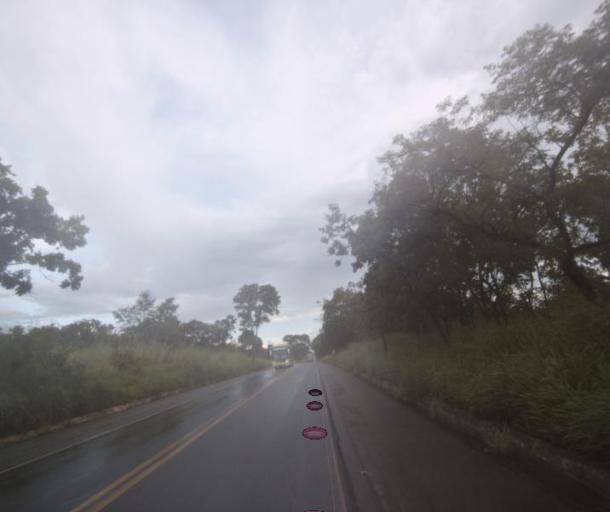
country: BR
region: Goias
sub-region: Porangatu
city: Porangatu
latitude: -13.8157
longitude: -49.0403
